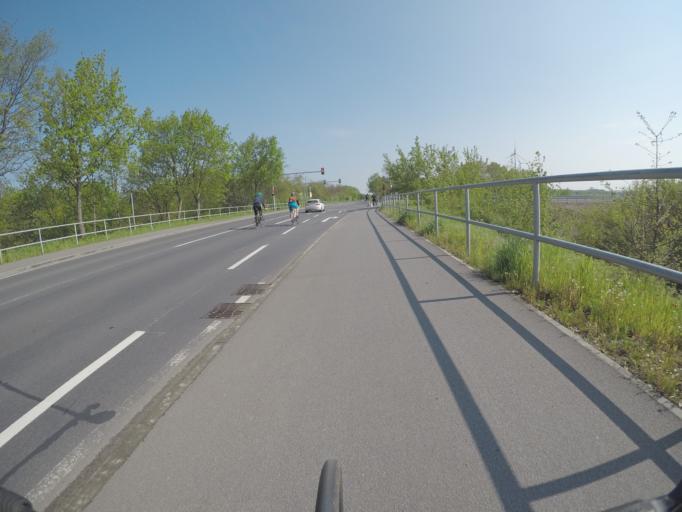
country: DE
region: Berlin
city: Buchholz
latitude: 52.6240
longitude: 13.4312
